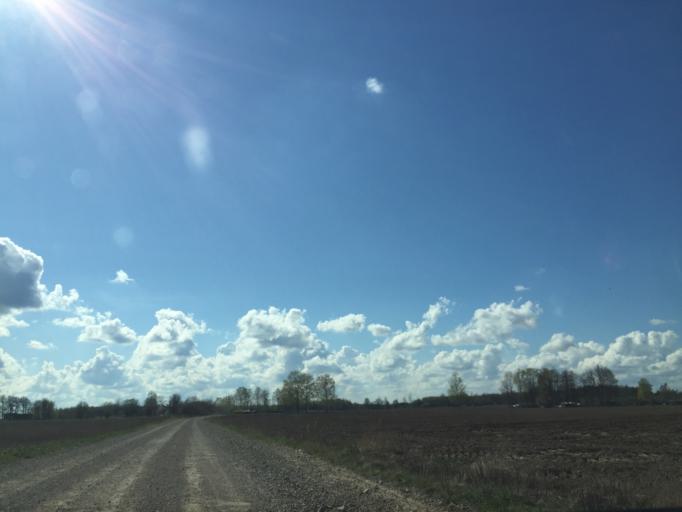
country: LV
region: Beverina
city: Murmuiza
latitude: 57.4835
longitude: 25.6249
